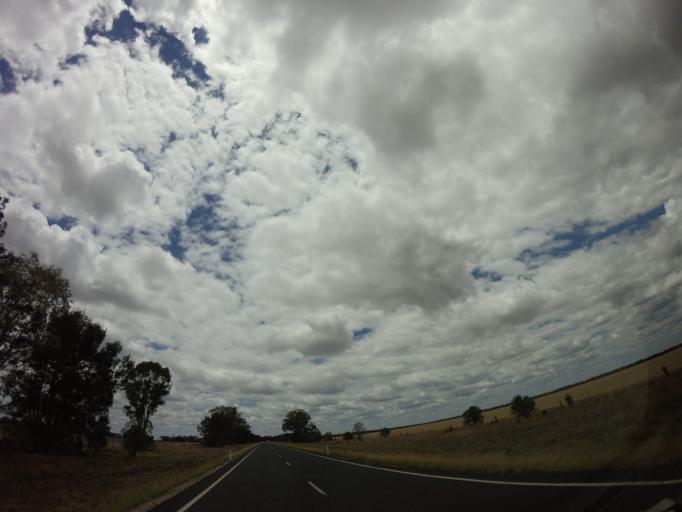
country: AU
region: Queensland
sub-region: Goondiwindi
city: Goondiwindi
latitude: -28.1655
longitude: 150.5316
